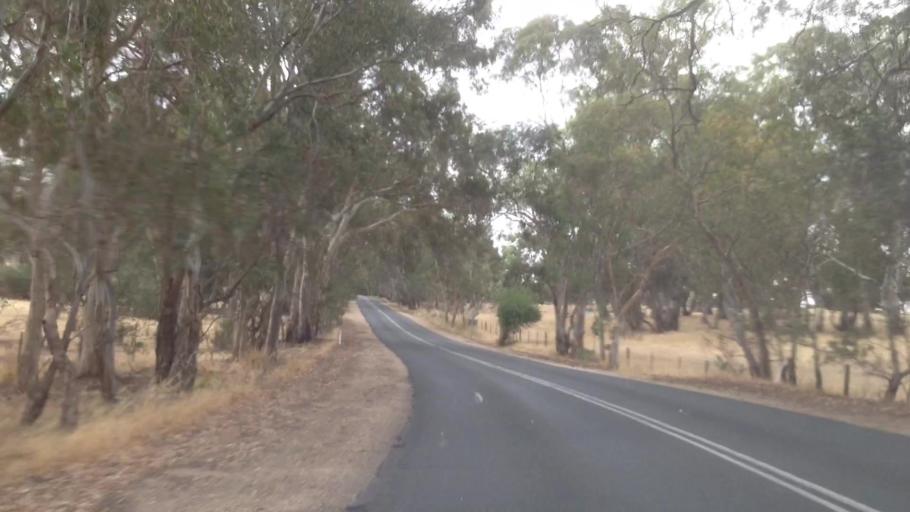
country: AU
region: South Australia
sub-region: Barossa
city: Williamstown
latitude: -34.6503
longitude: 138.8634
